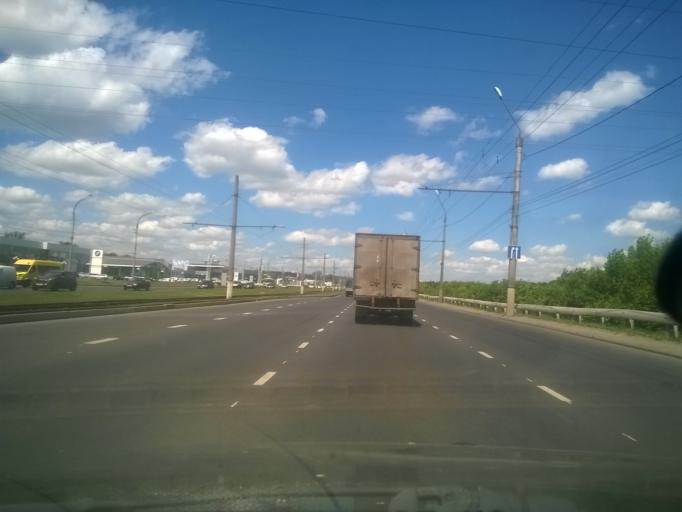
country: RU
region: Kursk
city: Kursk
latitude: 51.6850
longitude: 36.1517
